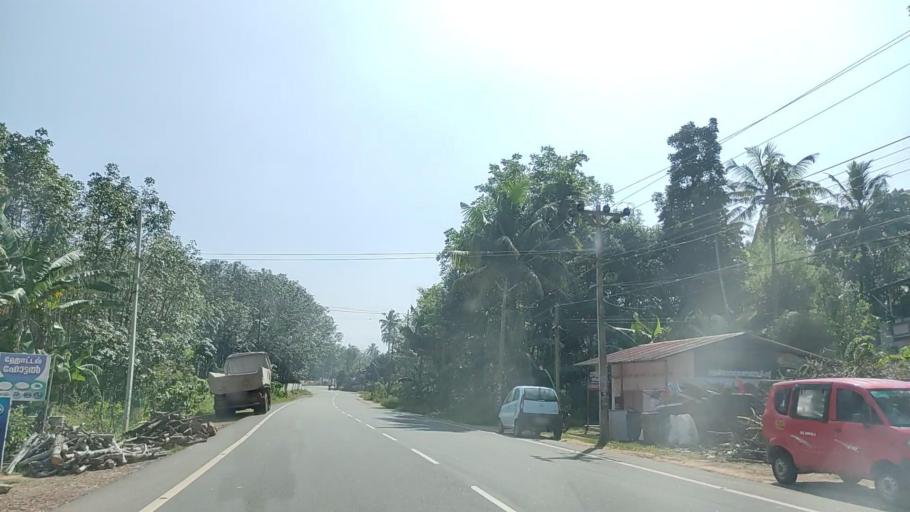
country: IN
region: Kerala
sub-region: Kollam
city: Punalur
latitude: 8.9180
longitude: 77.0403
